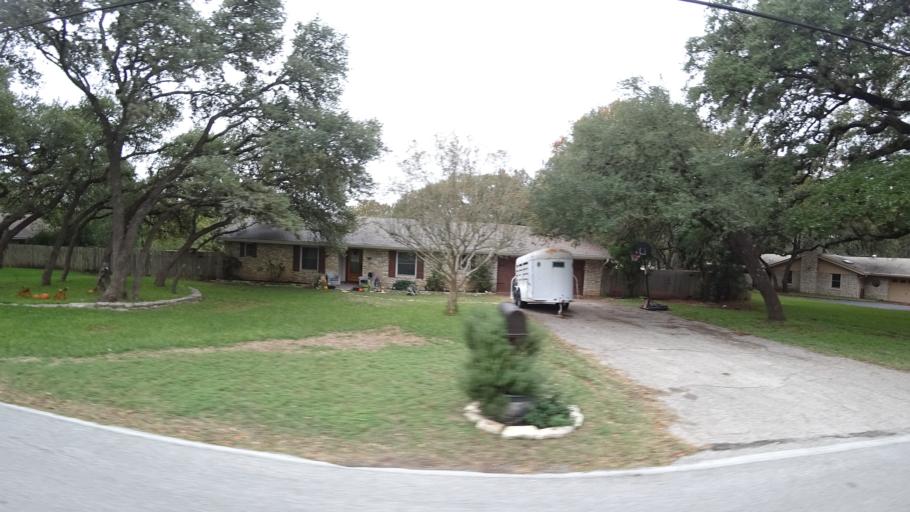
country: US
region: Texas
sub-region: Travis County
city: Shady Hollow
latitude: 30.2220
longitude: -97.9007
